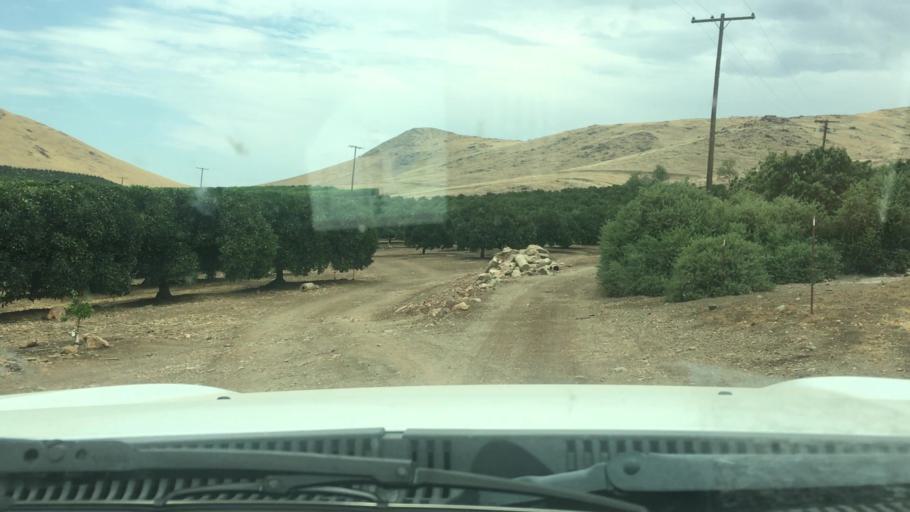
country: US
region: California
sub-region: Tulare County
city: Porterville
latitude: 36.0987
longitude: -119.0122
